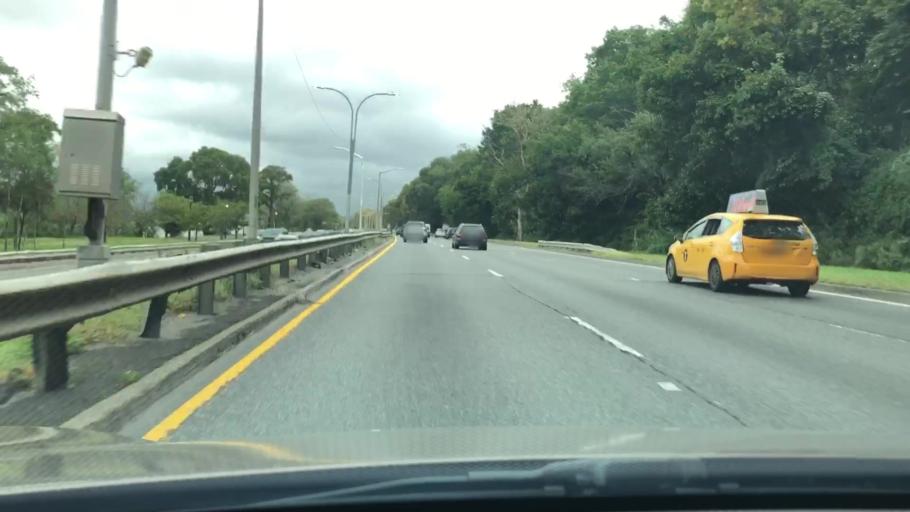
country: US
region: New Jersey
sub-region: Bergen County
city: Edgewater
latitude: 40.8070
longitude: -73.9697
